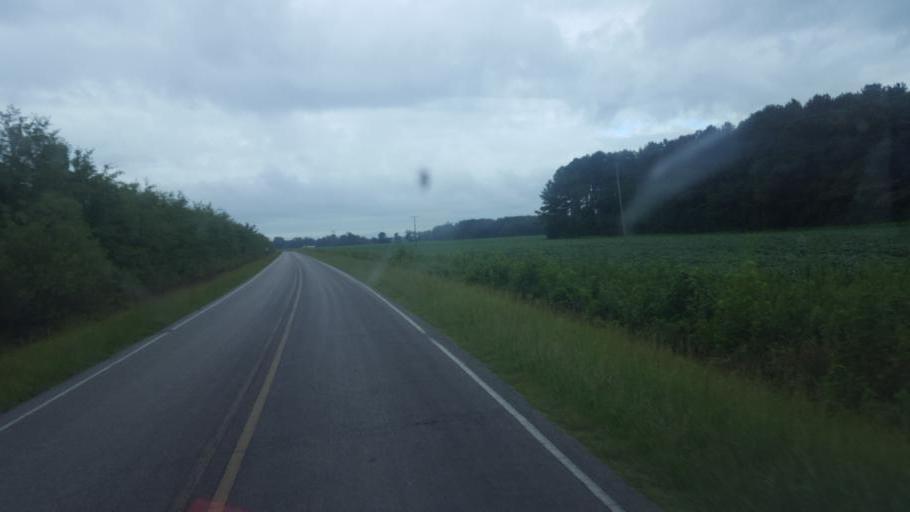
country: US
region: North Carolina
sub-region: Tyrrell County
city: Columbia
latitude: 35.9469
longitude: -76.2814
